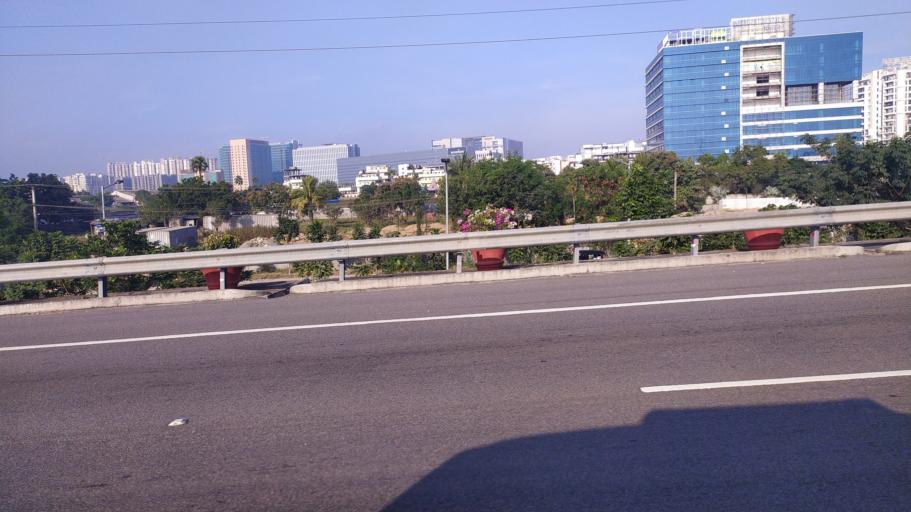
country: IN
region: Telangana
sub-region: Rangareddi
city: Kukatpalli
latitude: 17.4176
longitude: 78.3559
